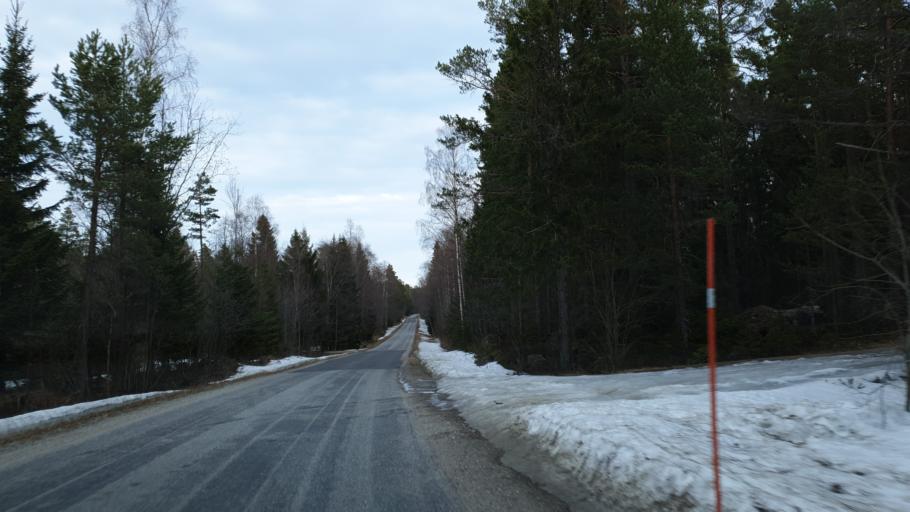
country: SE
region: Gaevleborg
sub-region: Nordanstigs Kommun
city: Bergsjoe
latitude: 61.9597
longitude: 17.3532
